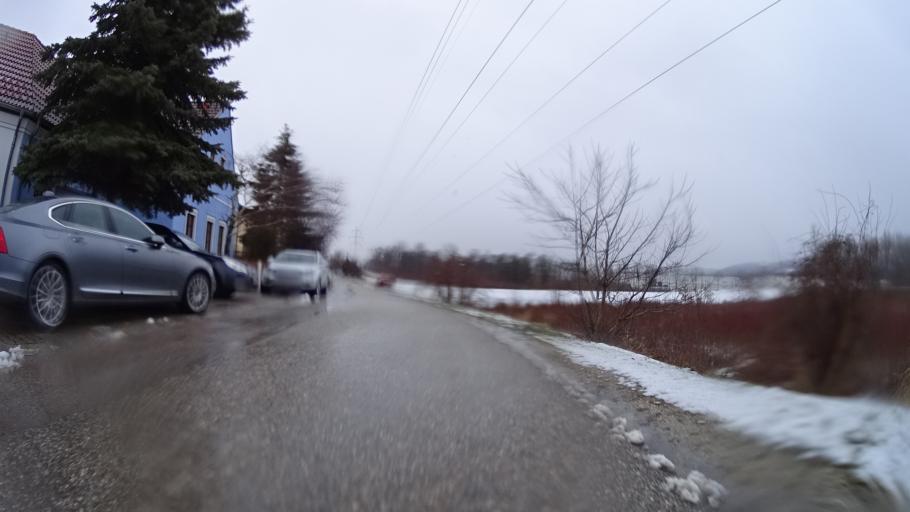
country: AT
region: Lower Austria
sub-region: Politischer Bezirk Korneuburg
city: Leobendorf
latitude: 48.3726
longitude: 16.2981
